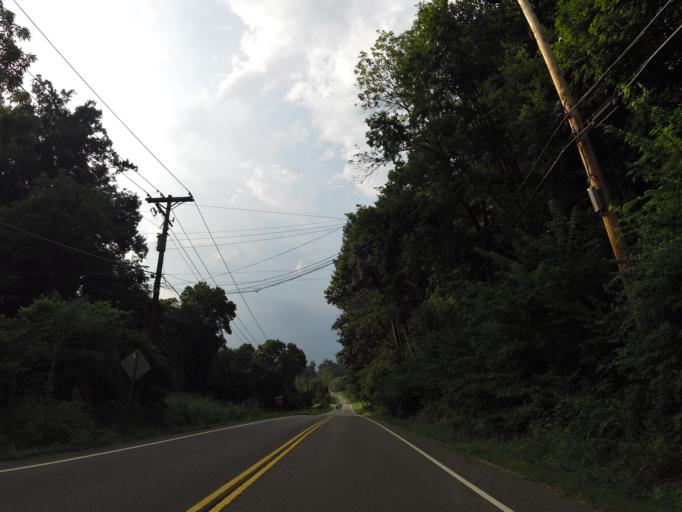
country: US
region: Tennessee
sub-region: Knox County
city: Knoxville
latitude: 35.8974
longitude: -83.9351
